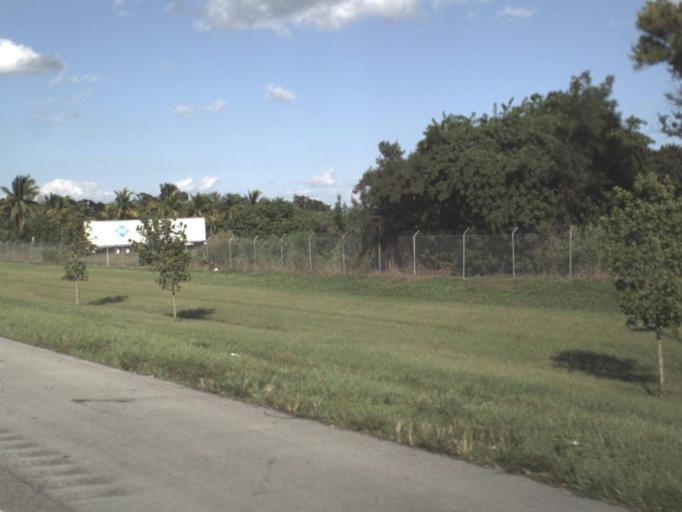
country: US
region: Florida
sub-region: Broward County
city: Lauderdale Lakes
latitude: 26.1806
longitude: -80.2187
